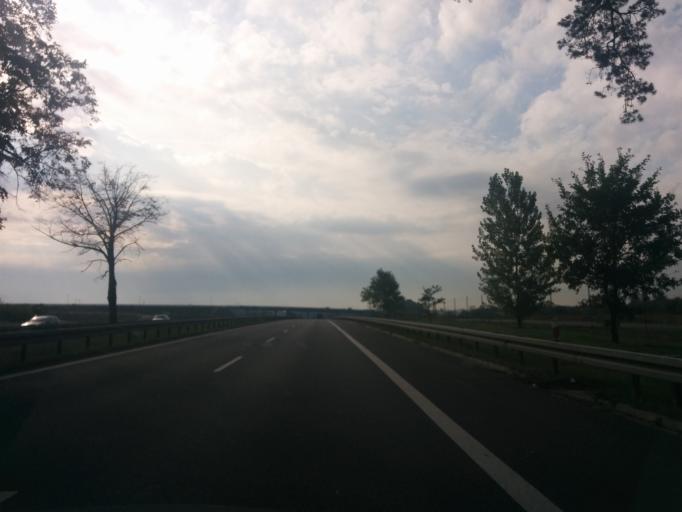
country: PL
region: Masovian Voivodeship
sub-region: Powiat bialobrzeski
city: Stara Blotnica
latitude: 51.5873
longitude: 20.9974
